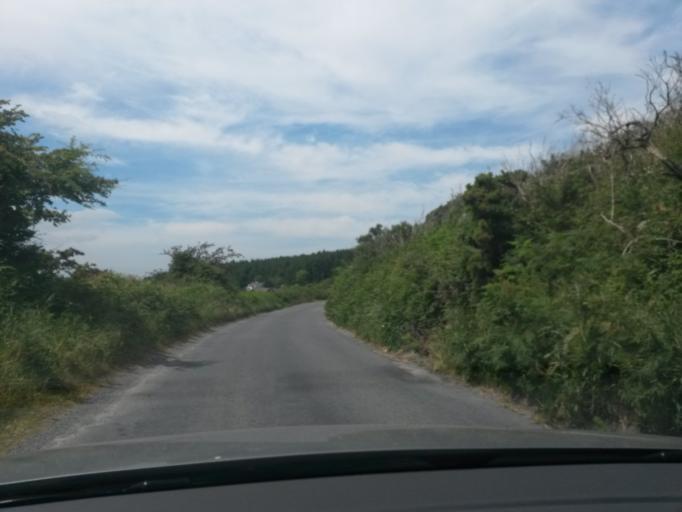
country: IE
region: Leinster
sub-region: Wicklow
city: Enniskerry
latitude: 53.1876
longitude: -6.2212
